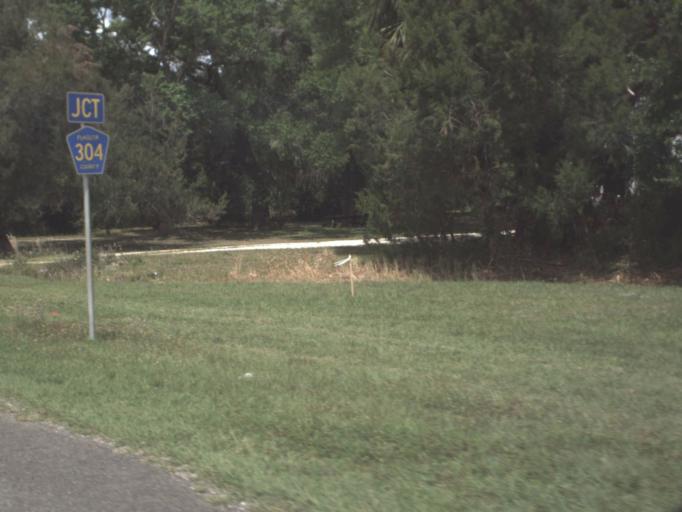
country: US
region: Florida
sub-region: Flagler County
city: Bunnell
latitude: 29.3420
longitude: -81.3109
